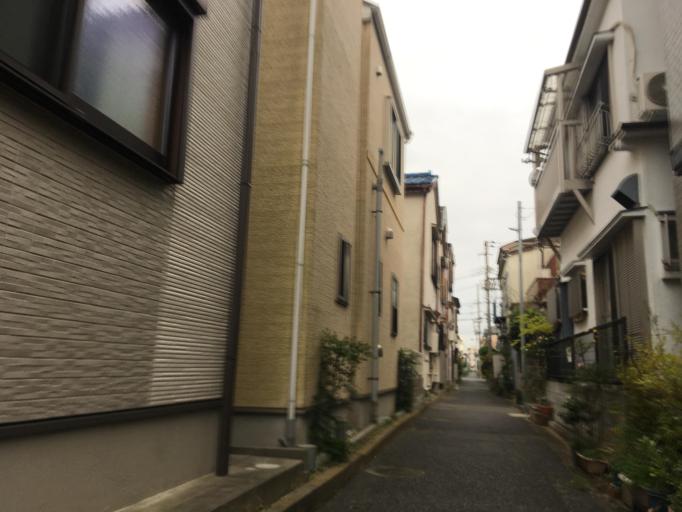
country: JP
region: Tokyo
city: Urayasu
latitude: 35.6760
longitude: 139.8844
